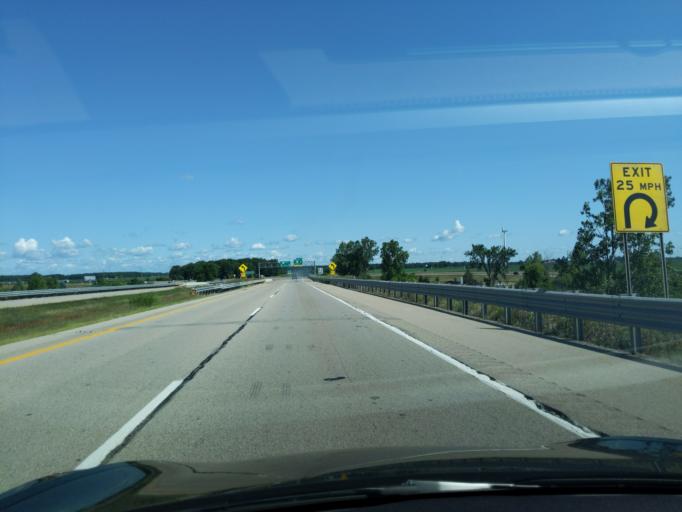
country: US
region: Michigan
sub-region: Gratiot County
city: Ithaca
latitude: 43.2900
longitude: -84.5821
